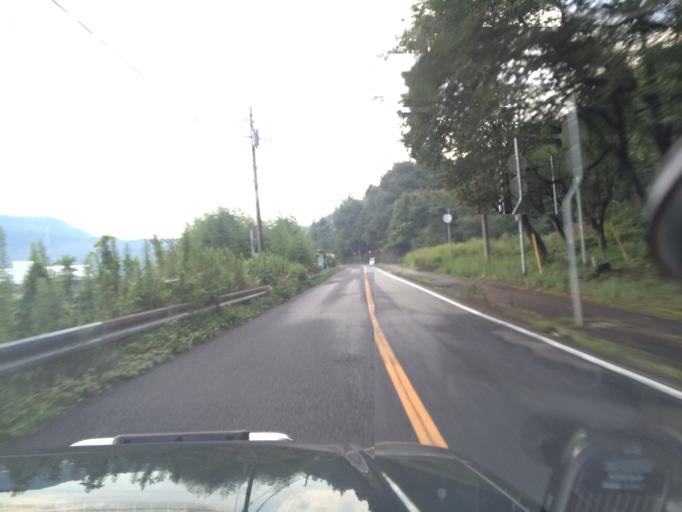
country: JP
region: Hyogo
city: Nishiwaki
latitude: 35.0975
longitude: 134.9966
